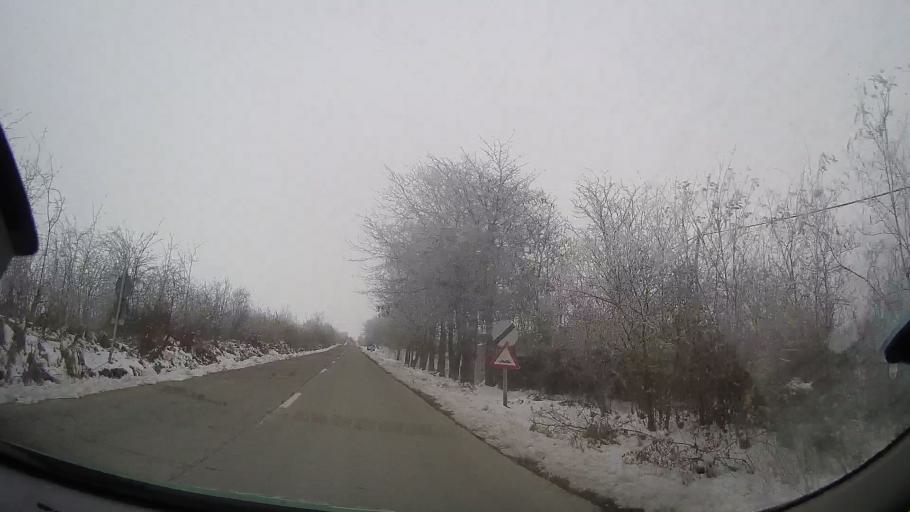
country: RO
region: Bacau
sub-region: Comuna Podu Turcului
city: Podu Turcului
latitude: 46.2057
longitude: 27.3978
